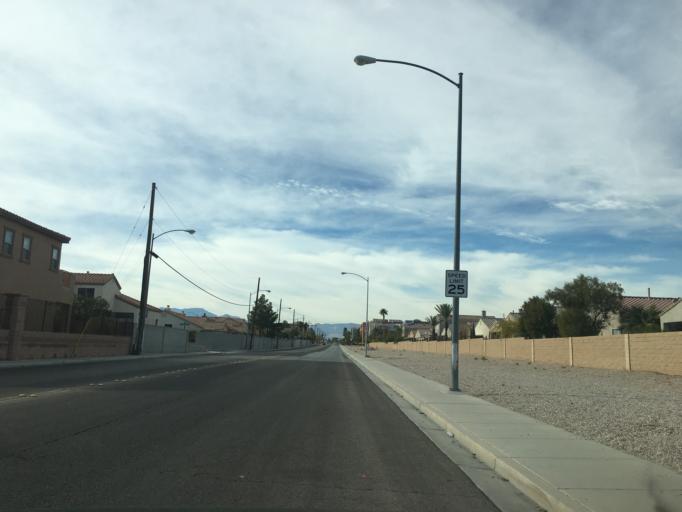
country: US
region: Nevada
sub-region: Clark County
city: Enterprise
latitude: 36.0208
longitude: -115.1640
